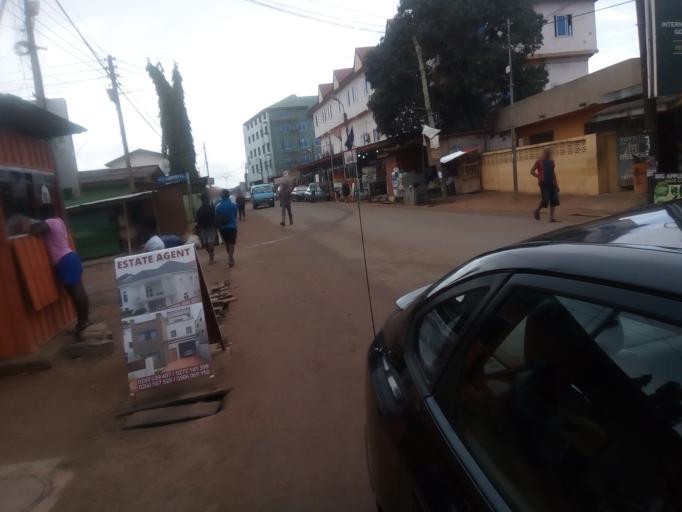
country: GH
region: Greater Accra
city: Dome
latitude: 5.6060
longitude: -0.2539
